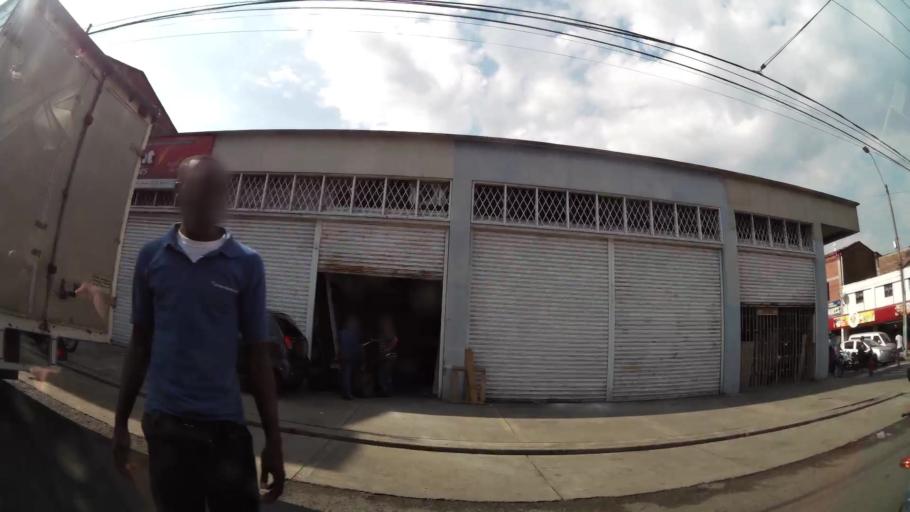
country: CO
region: Valle del Cauca
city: Cali
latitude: 3.4560
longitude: -76.5251
